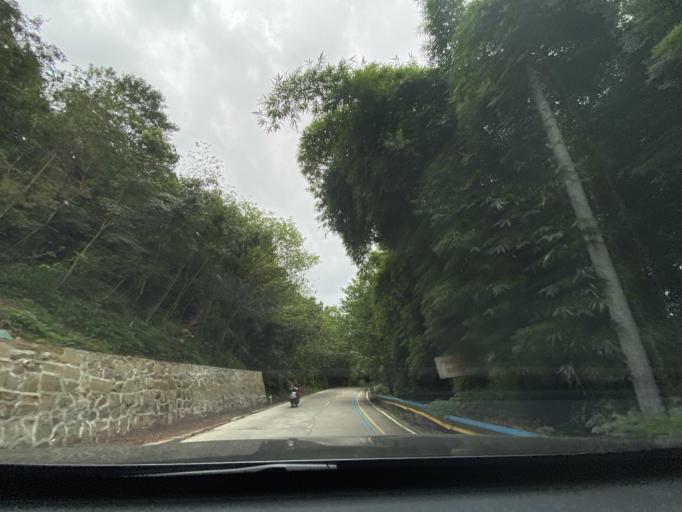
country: CN
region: Sichuan
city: Dongsheng
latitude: 30.4064
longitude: 104.0048
